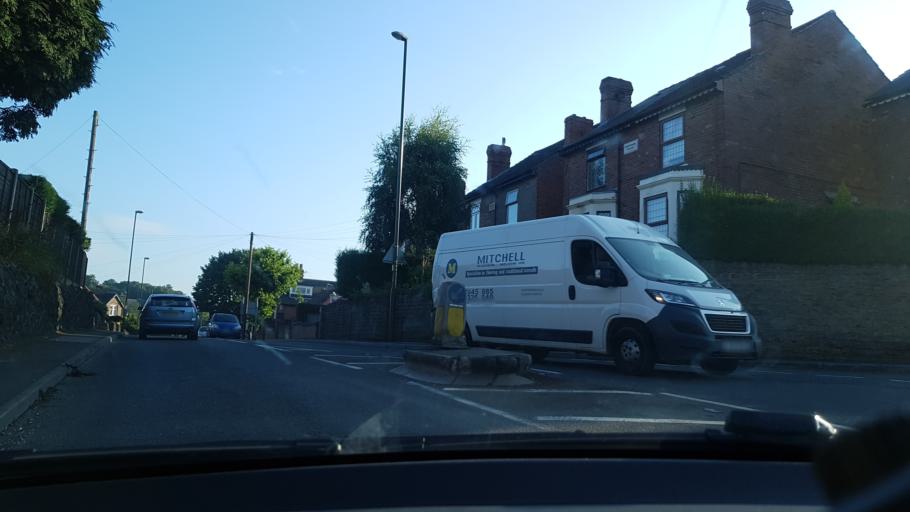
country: GB
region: England
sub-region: Derbyshire
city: Ilkeston
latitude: 52.9602
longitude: -1.3071
